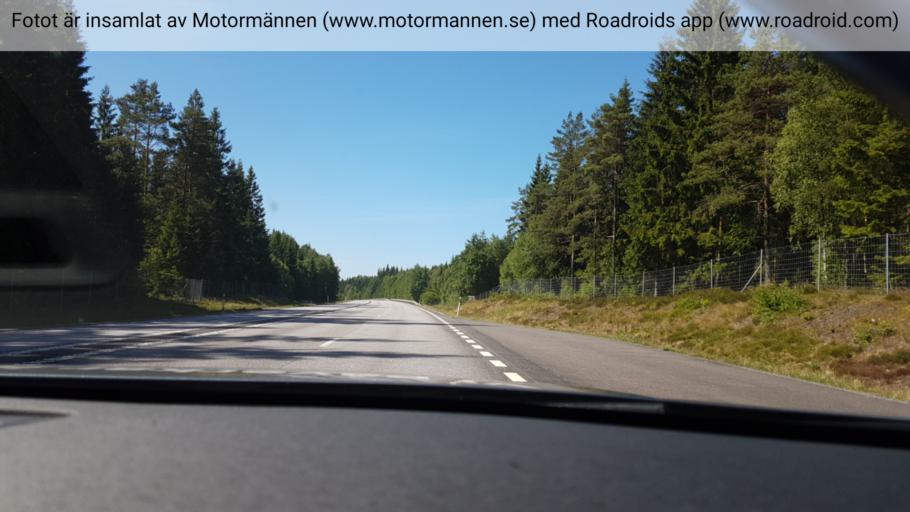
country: SE
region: Vaestra Goetaland
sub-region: Boras Kommun
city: Viskafors
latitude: 57.6236
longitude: 12.8873
